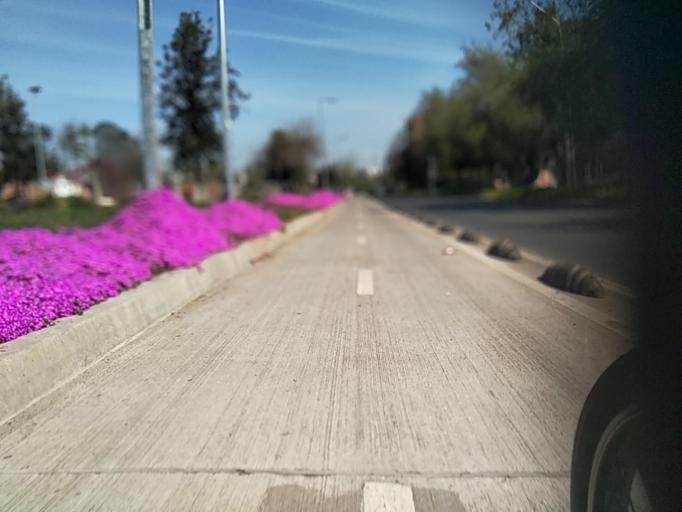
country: CL
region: Santiago Metropolitan
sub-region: Provincia de Santiago
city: Villa Presidente Frei, Nunoa, Santiago, Chile
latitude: -33.5004
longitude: -70.6059
